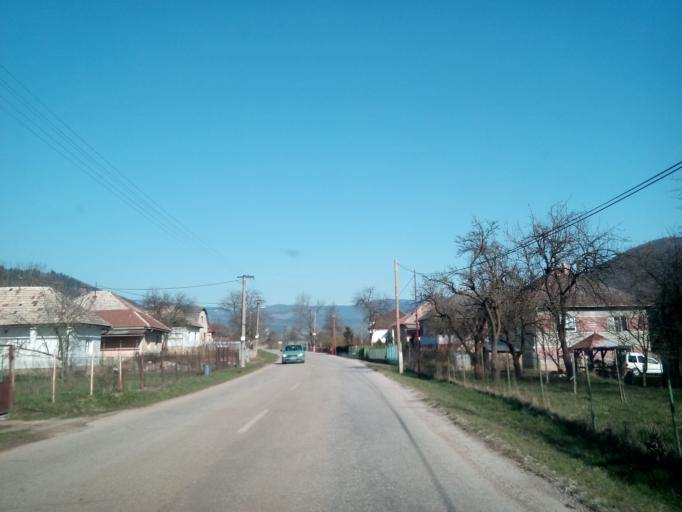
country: SK
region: Kosicky
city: Dobsina
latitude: 48.6859
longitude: 20.3260
